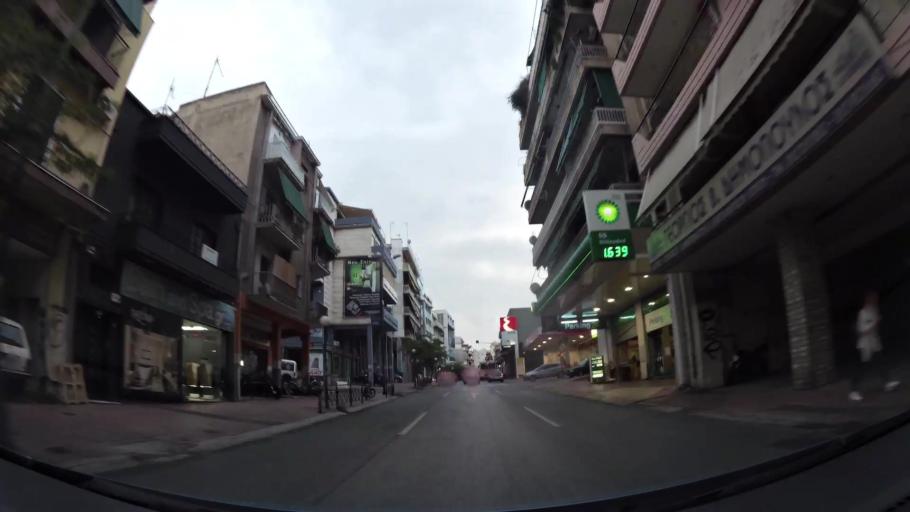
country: GR
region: Attica
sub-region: Nomarchia Athinas
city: Dhafni
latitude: 37.9613
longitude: 23.7342
